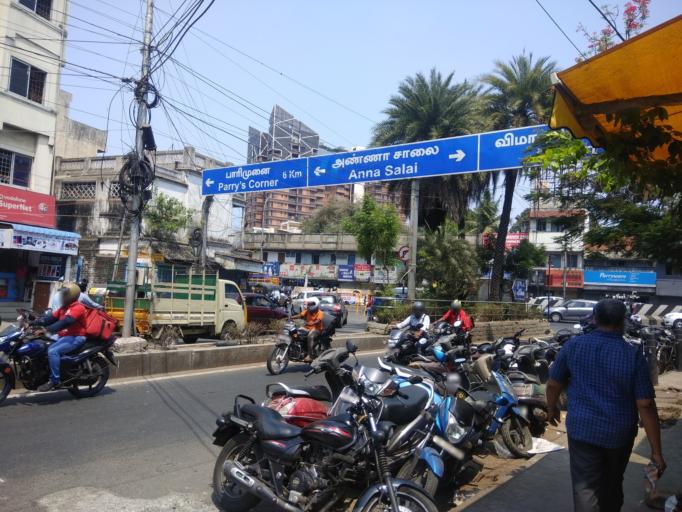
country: IN
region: Tamil Nadu
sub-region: Chennai
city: Chetput
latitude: 13.0561
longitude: 80.2555
